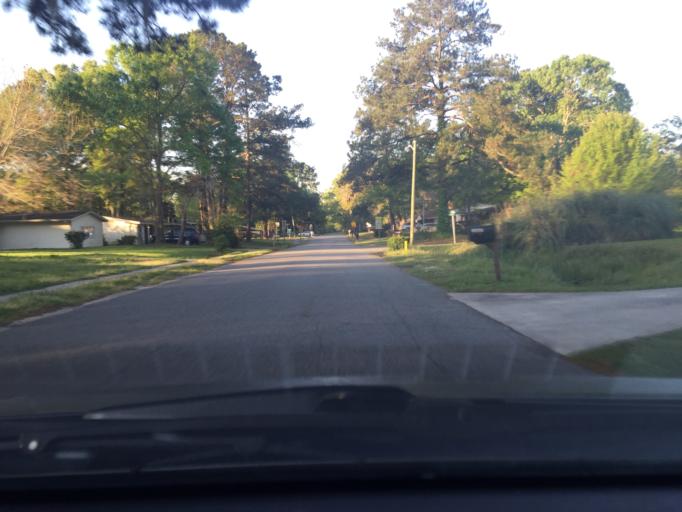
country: US
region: Georgia
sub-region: Chatham County
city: Montgomery
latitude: 31.9748
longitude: -81.1466
